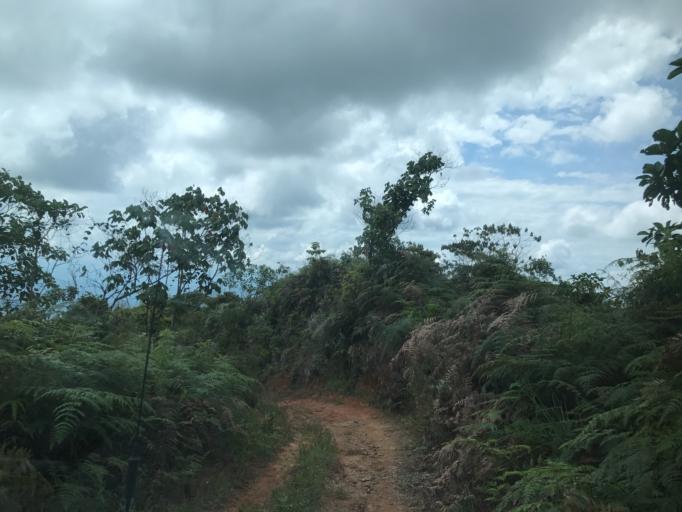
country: CO
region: Valle del Cauca
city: Obando
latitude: 4.5783
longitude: -75.8910
